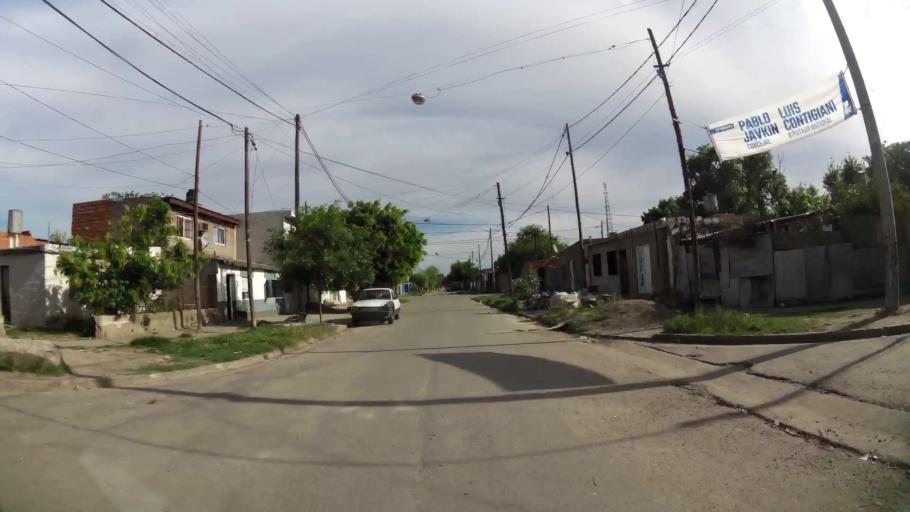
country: AR
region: Santa Fe
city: Granadero Baigorria
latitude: -32.9237
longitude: -60.7075
